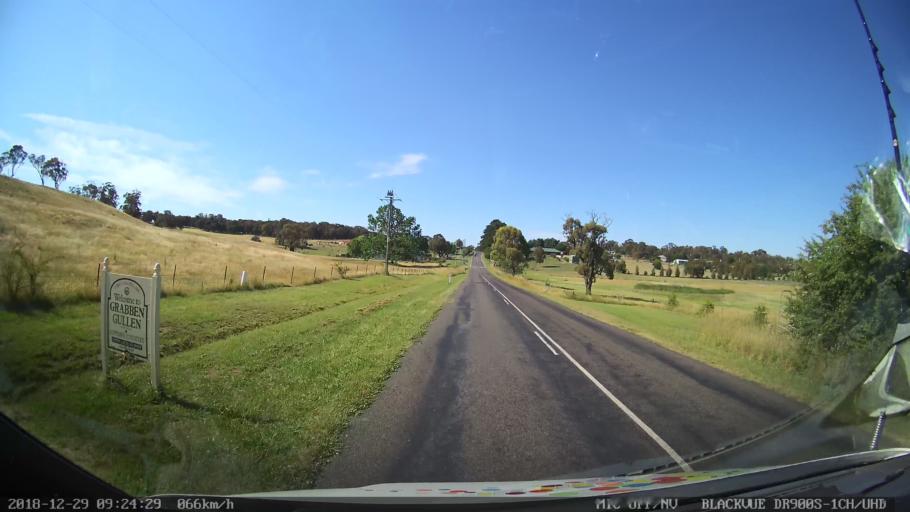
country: AU
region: New South Wales
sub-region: Upper Lachlan Shire
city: Crookwell
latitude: -34.5367
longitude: 149.3942
